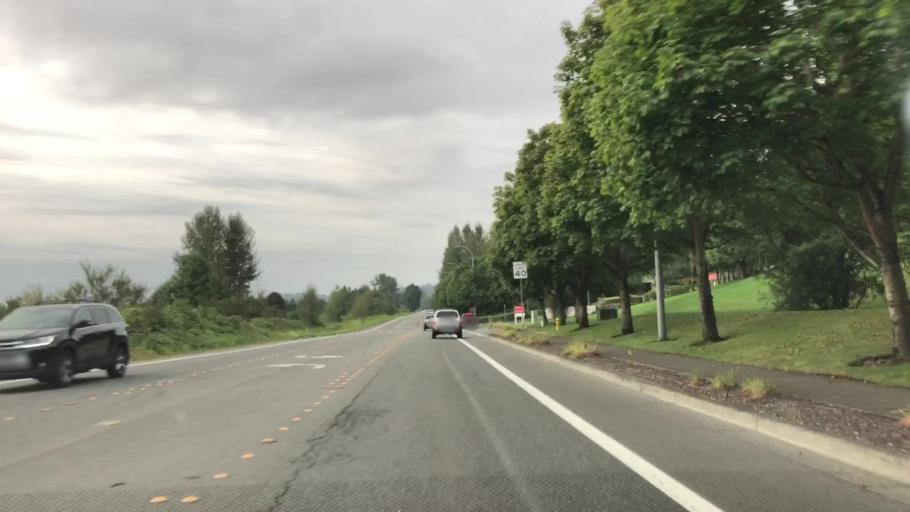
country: US
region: Washington
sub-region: King County
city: Kingsgate
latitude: 47.7030
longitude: -122.1530
